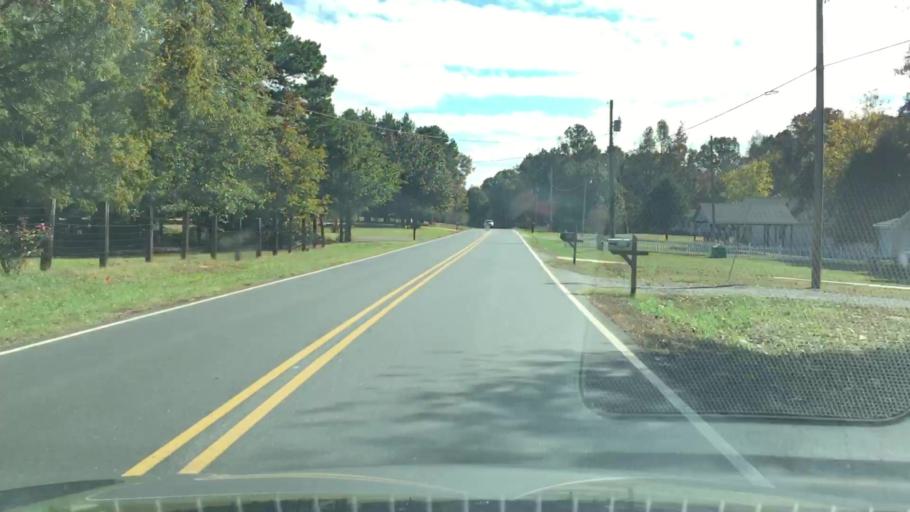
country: US
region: North Carolina
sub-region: Gaston County
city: Davidson
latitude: 35.5362
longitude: -80.8288
